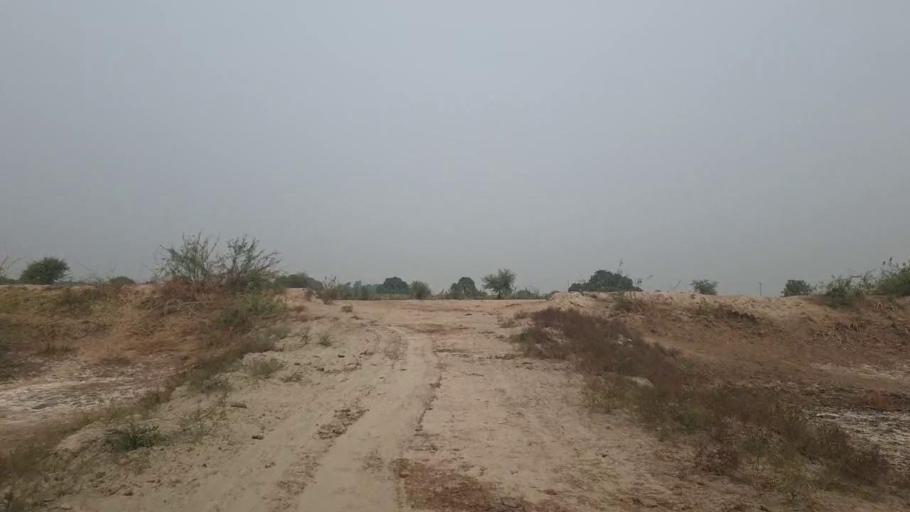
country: PK
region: Sindh
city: Tando Adam
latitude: 25.7889
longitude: 68.6649
